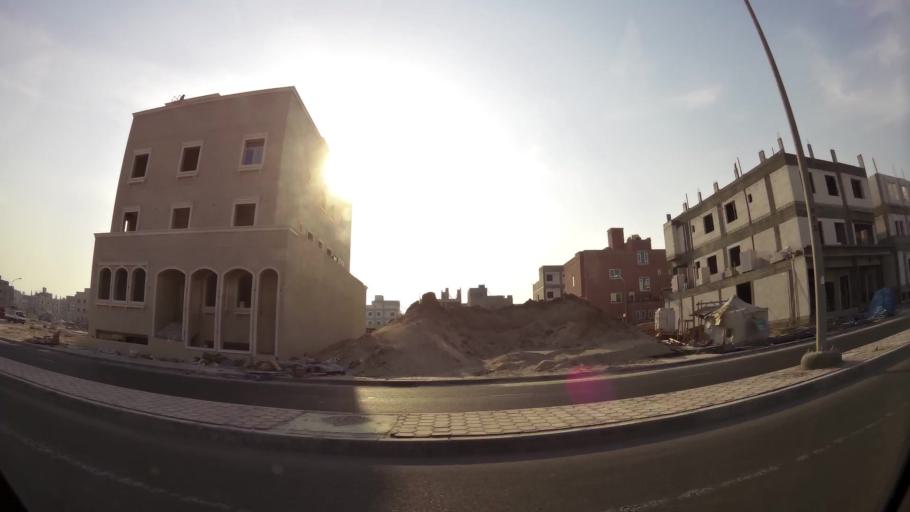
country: KW
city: Al Funaytis
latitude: 29.2221
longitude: 48.0924
